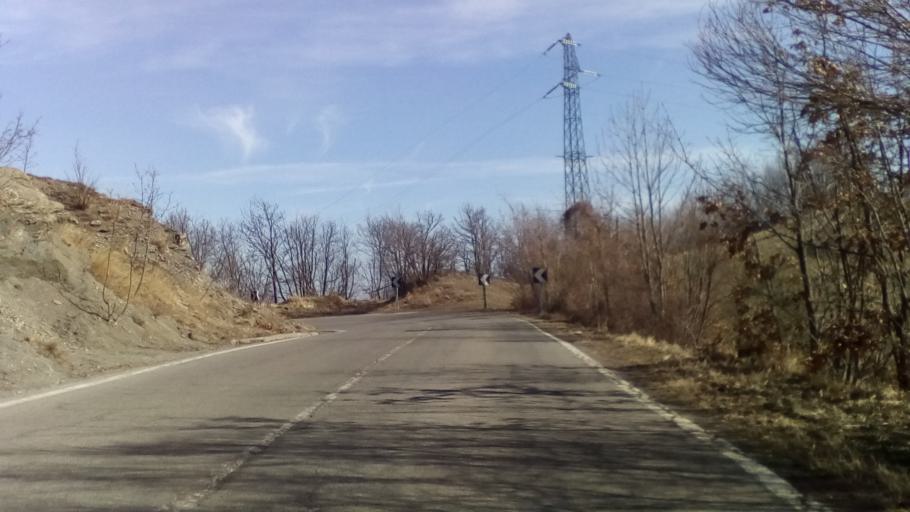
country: IT
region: Emilia-Romagna
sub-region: Provincia di Modena
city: Riolunato
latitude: 44.2272
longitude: 10.6286
